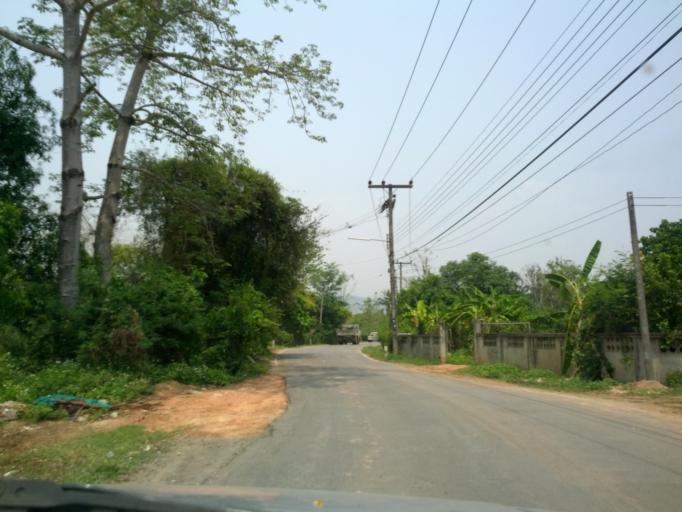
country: TH
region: Chiang Mai
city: San Sai
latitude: 18.8938
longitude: 99.0835
